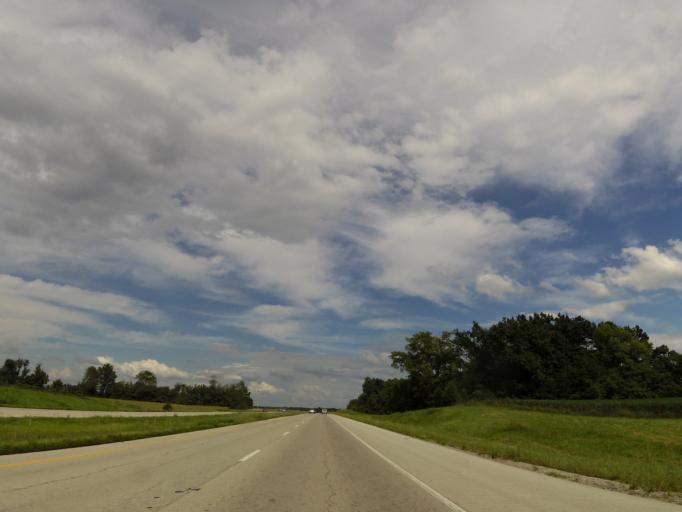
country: US
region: Kentucky
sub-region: Trigg County
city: Cadiz
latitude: 36.8811
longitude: -87.6705
